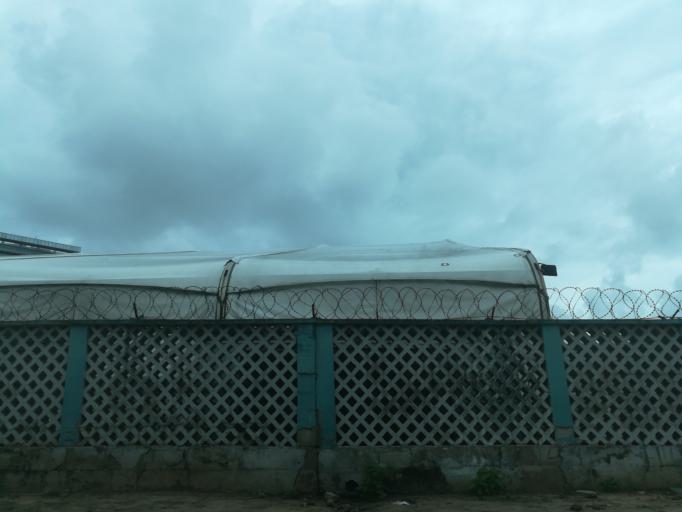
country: NG
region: Lagos
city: Lagos
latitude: 6.4367
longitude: 3.4104
